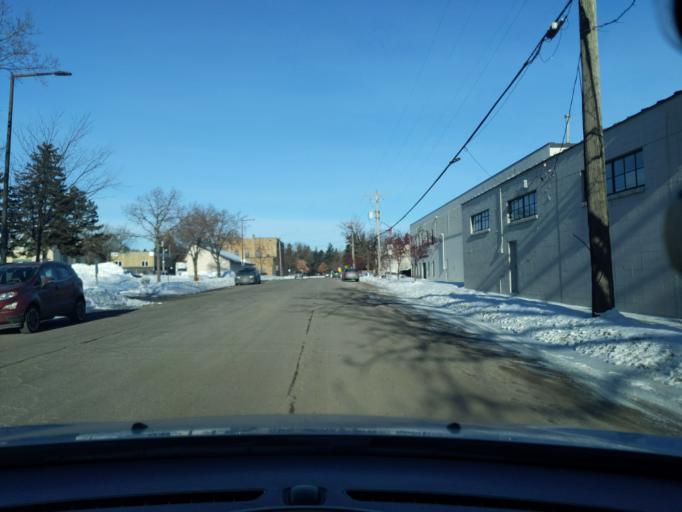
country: US
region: Minnesota
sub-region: Ramsey County
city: Lauderdale
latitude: 44.9684
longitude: -93.1959
